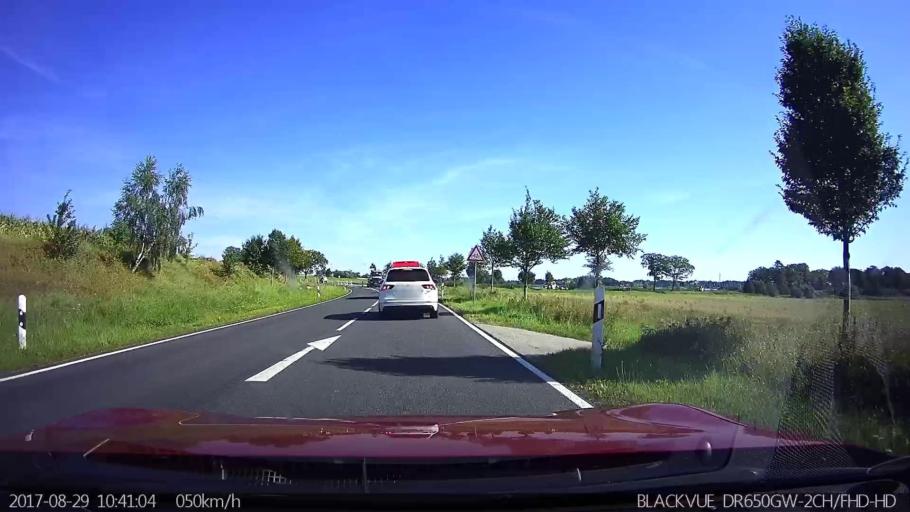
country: DE
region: Mecklenburg-Vorpommern
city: Franzburg
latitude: 54.1895
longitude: 12.8636
